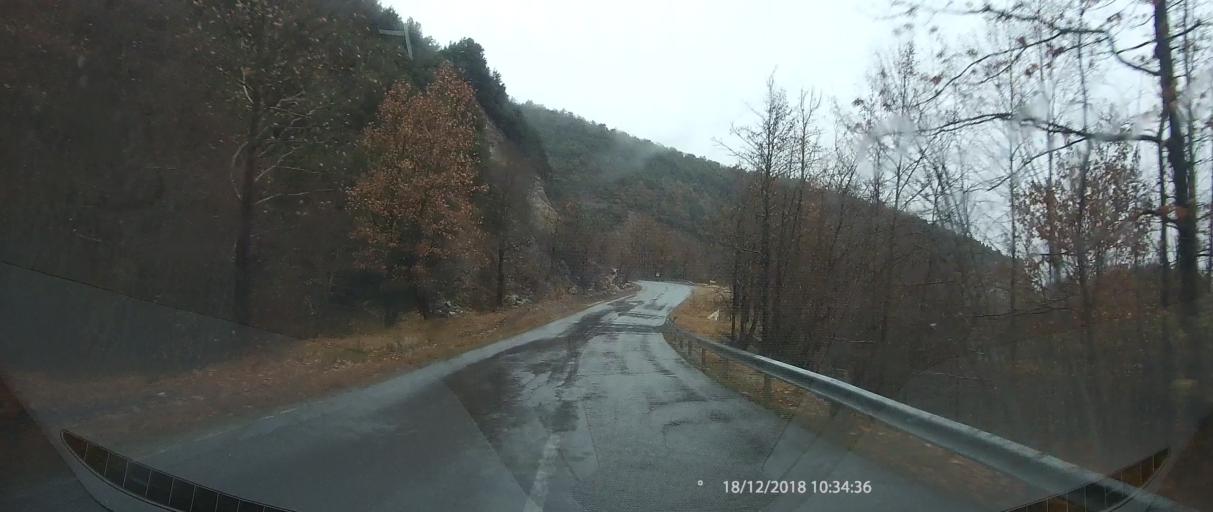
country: GR
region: Central Macedonia
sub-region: Nomos Pierias
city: Kato Milia
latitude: 40.2087
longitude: 22.3016
